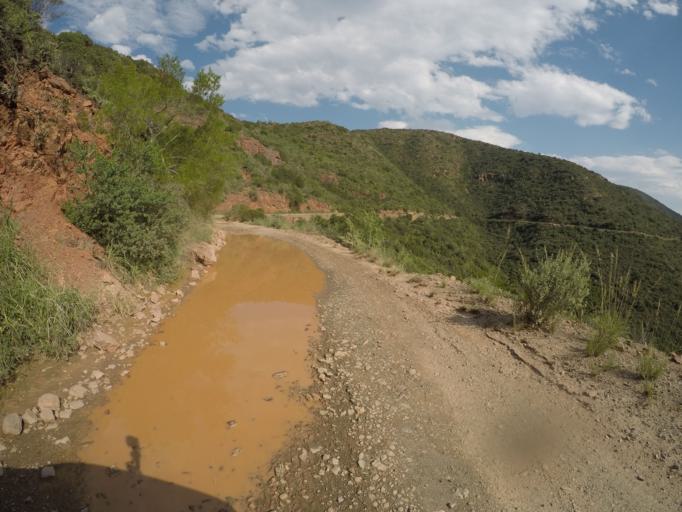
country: ZA
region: Eastern Cape
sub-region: Cacadu District Municipality
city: Kareedouw
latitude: -33.6473
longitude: 24.3448
